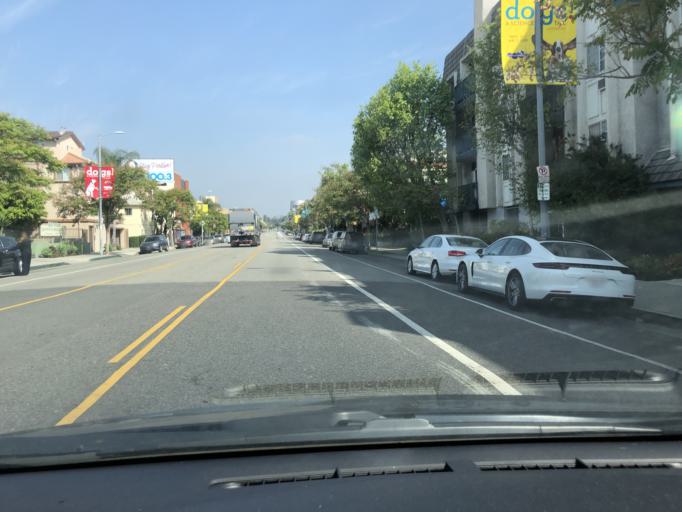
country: US
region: California
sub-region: Los Angeles County
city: Culver City
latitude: 34.0233
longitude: -118.4061
